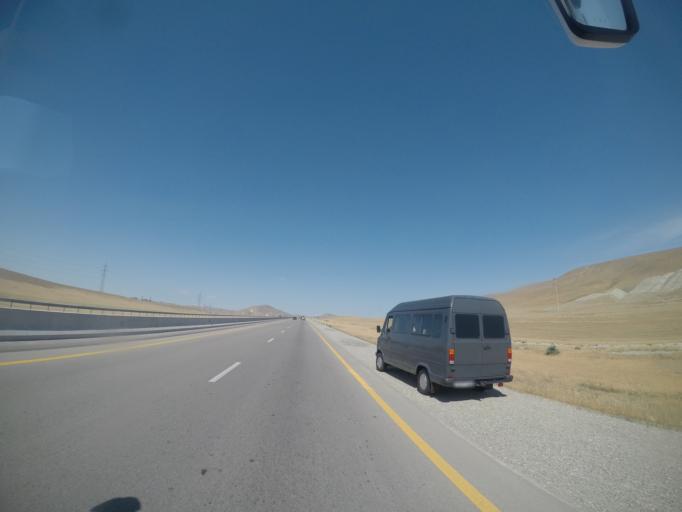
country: AZ
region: Sumqayit
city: Haci Zeynalabdin
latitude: 40.4946
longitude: 49.3368
